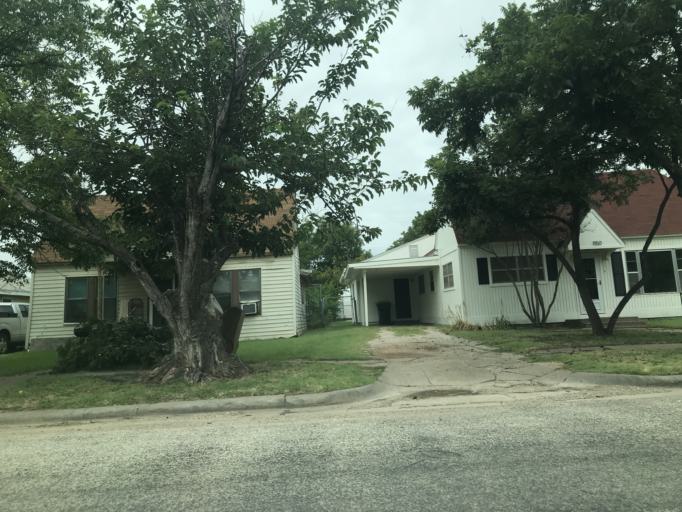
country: US
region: Texas
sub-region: Taylor County
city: Abilene
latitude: 32.4362
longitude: -99.7374
